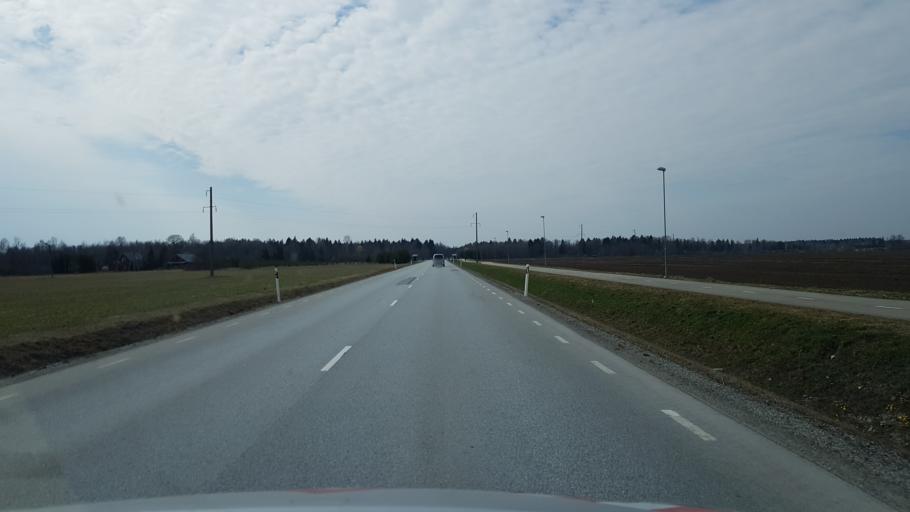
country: EE
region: Ida-Virumaa
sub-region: Aseri vald
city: Aseri
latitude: 59.3540
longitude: 26.8742
